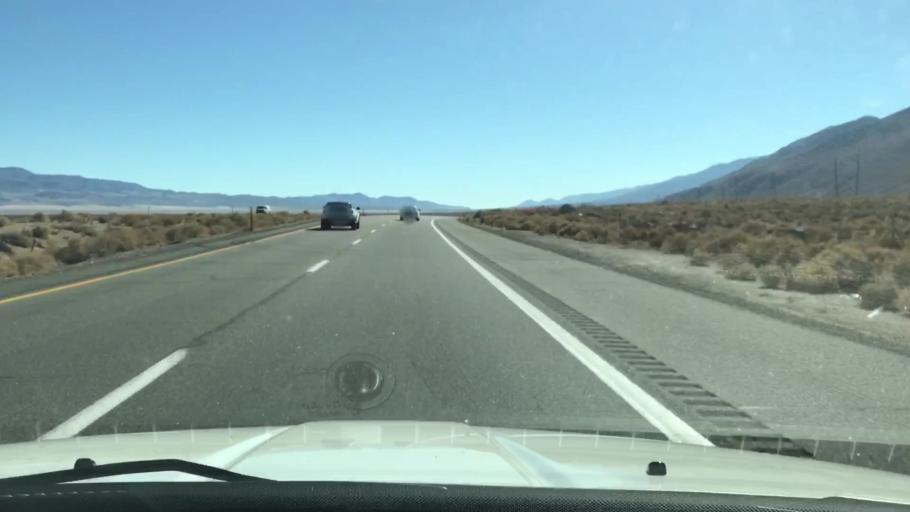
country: US
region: California
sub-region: Inyo County
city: Lone Pine
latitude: 36.4328
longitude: -118.0322
